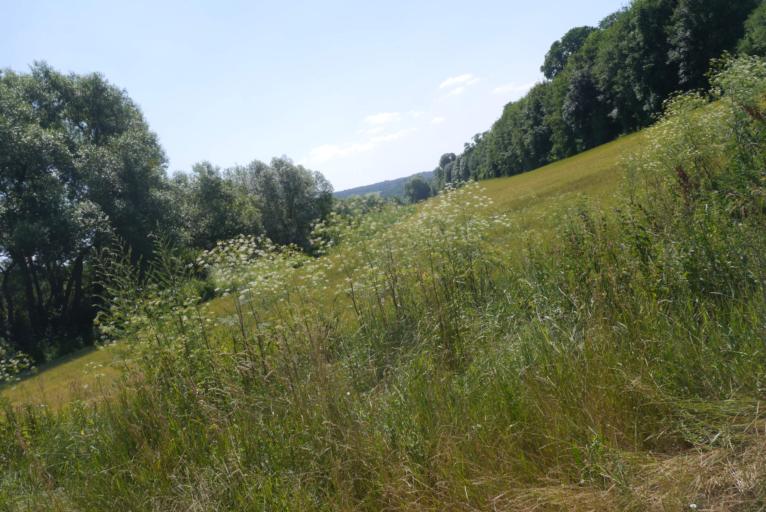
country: HU
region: Komarom-Esztergom
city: Bajna
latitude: 47.5786
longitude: 18.5924
